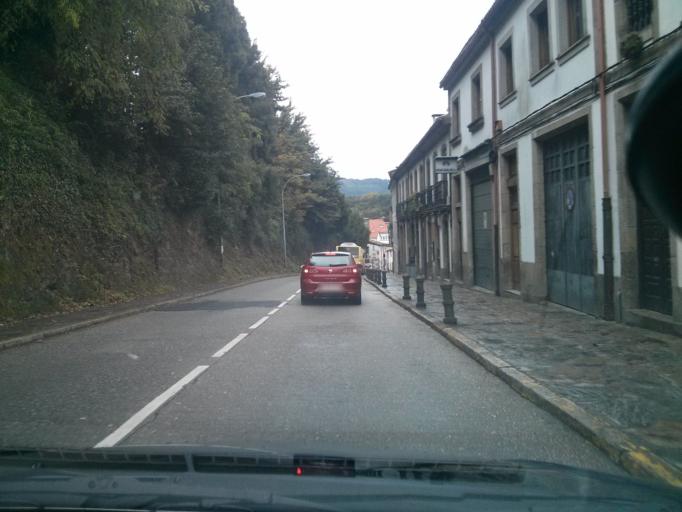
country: ES
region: Galicia
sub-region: Provincia da Coruna
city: Santiago de Compostela
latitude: 42.8794
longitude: -8.5488
